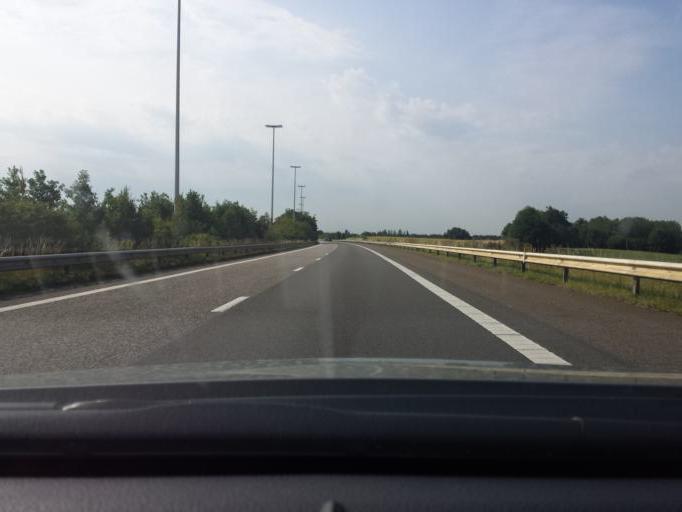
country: BE
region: Flanders
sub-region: Provincie Limburg
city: Hoeselt
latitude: 50.8033
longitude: 5.5197
